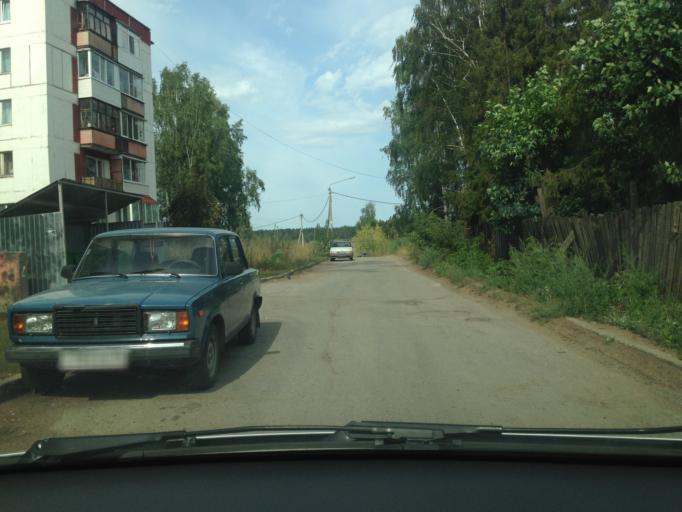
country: RU
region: Udmurtiya
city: Izhevsk
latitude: 56.8753
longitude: 53.1969
